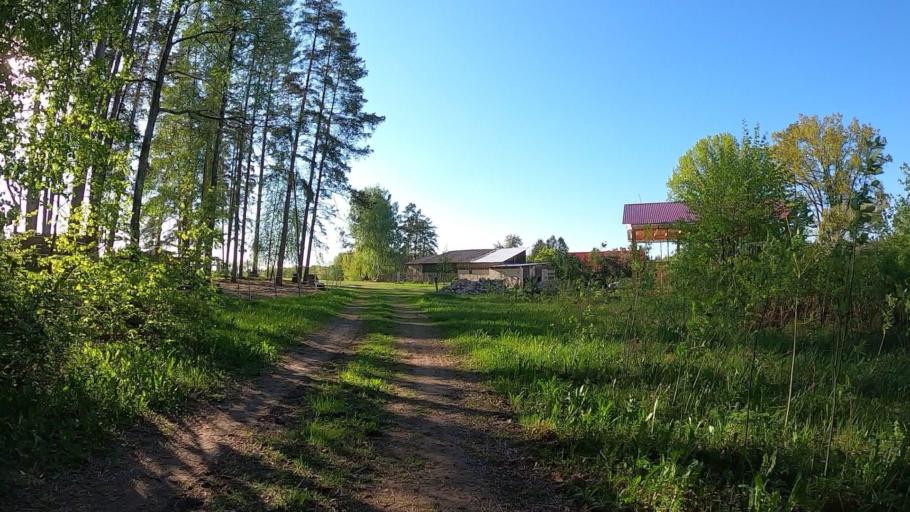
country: LV
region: Baldone
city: Baldone
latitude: 56.7730
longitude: 24.3415
